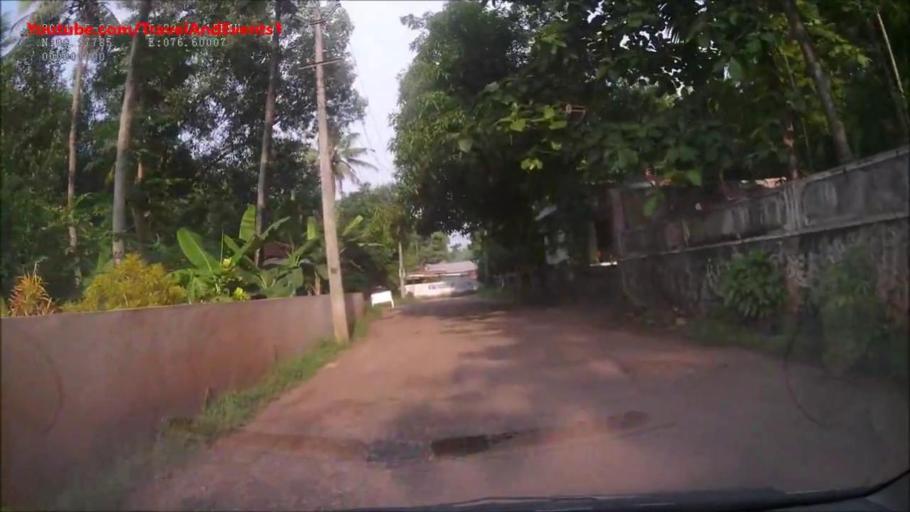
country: IN
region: Kerala
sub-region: Ernakulam
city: Muvattupula
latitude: 9.9731
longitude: 76.6047
